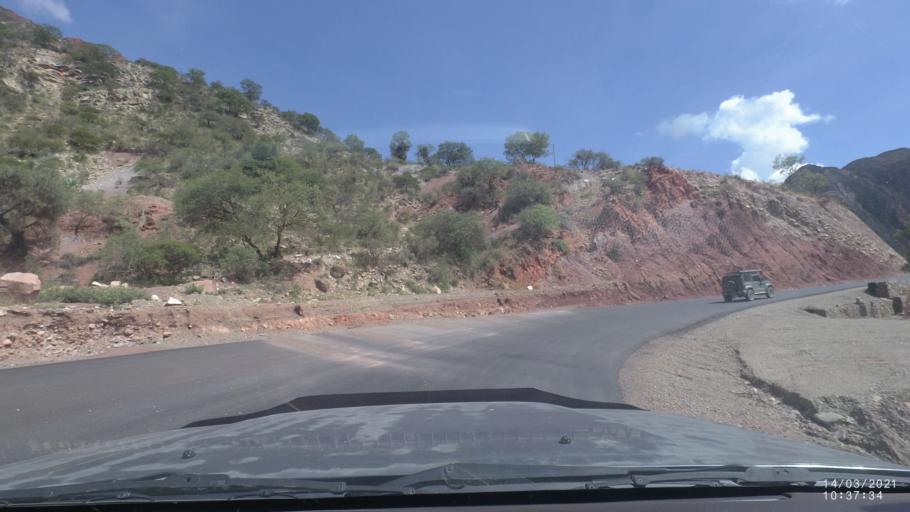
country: BO
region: Cochabamba
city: Cliza
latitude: -17.8987
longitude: -65.8894
